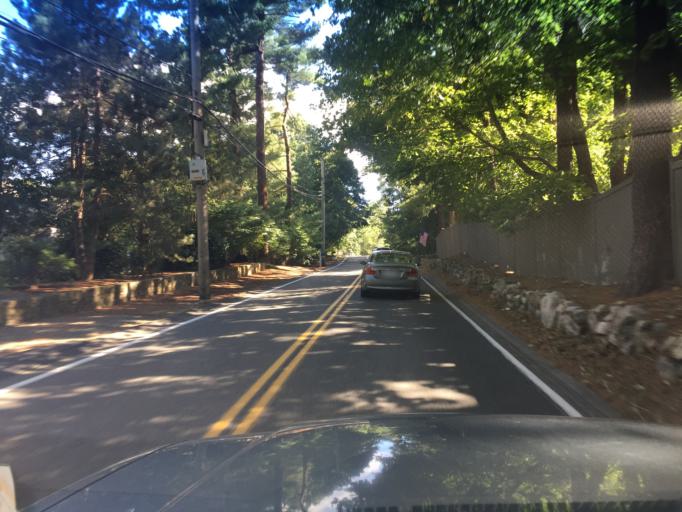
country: US
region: Massachusetts
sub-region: Norfolk County
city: Dover
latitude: 42.2577
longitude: -71.2721
